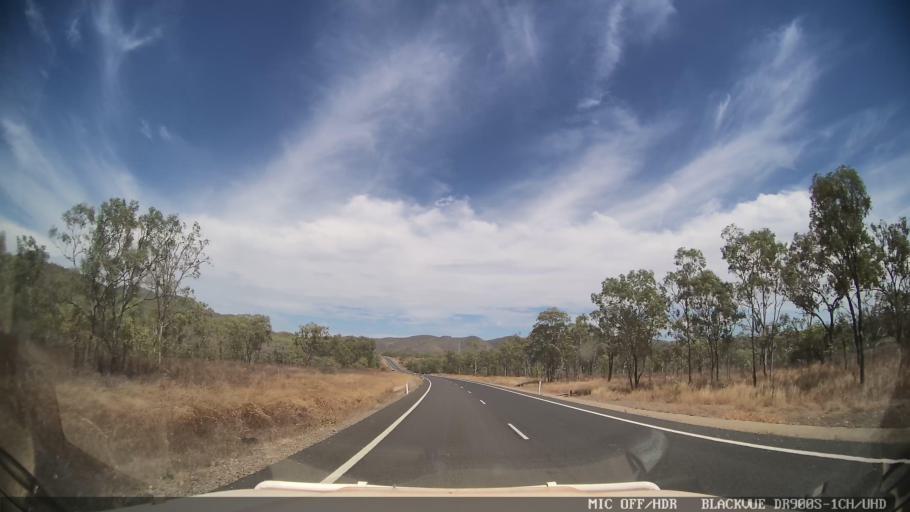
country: AU
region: Queensland
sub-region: Cook
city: Cooktown
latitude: -15.9345
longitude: 144.8391
